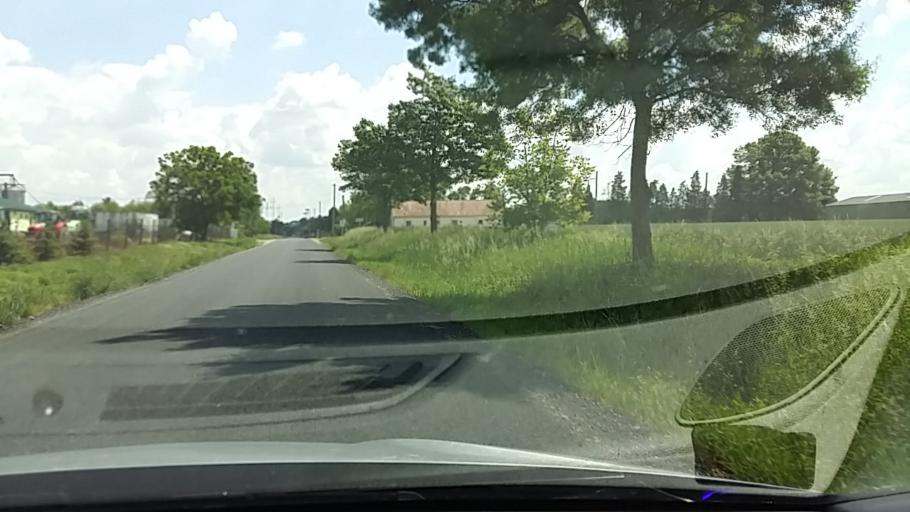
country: HU
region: Vas
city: Kormend
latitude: 46.9657
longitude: 16.5988
